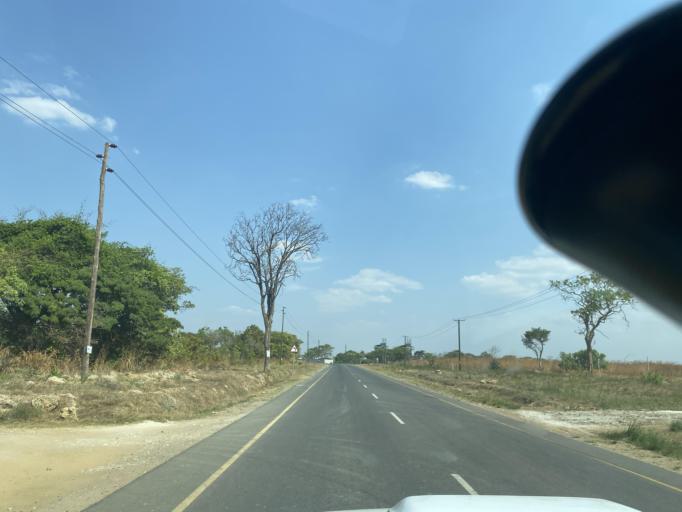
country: ZM
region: Lusaka
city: Lusaka
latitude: -15.3385
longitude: 28.0755
